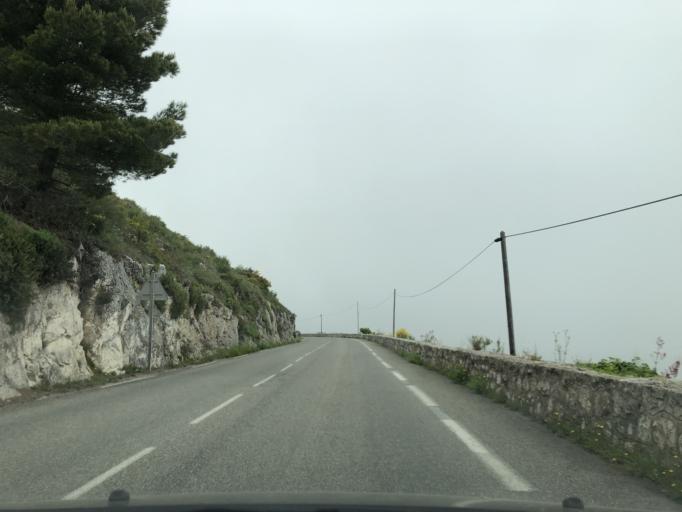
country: FR
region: Provence-Alpes-Cote d'Azur
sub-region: Departement des Alpes-Maritimes
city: Beaulieu-sur-Mer
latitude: 43.7269
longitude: 7.3437
